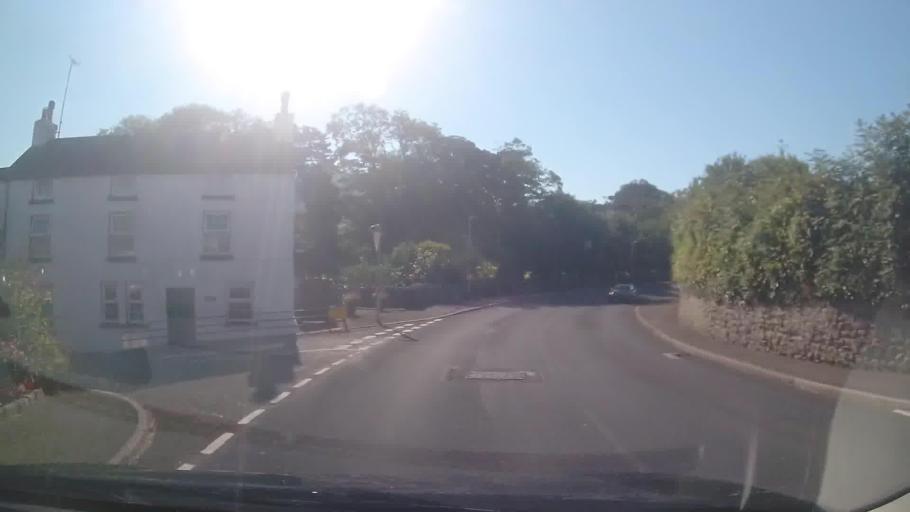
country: GB
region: England
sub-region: Cumbria
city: Millom
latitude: 54.2818
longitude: -3.3706
